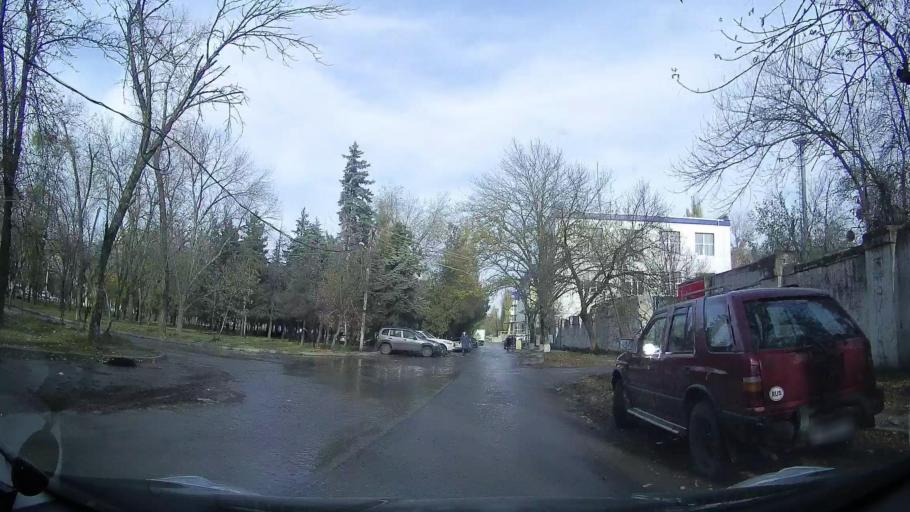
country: RU
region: Rostov
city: Severnyy
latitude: 47.2659
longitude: 39.7229
